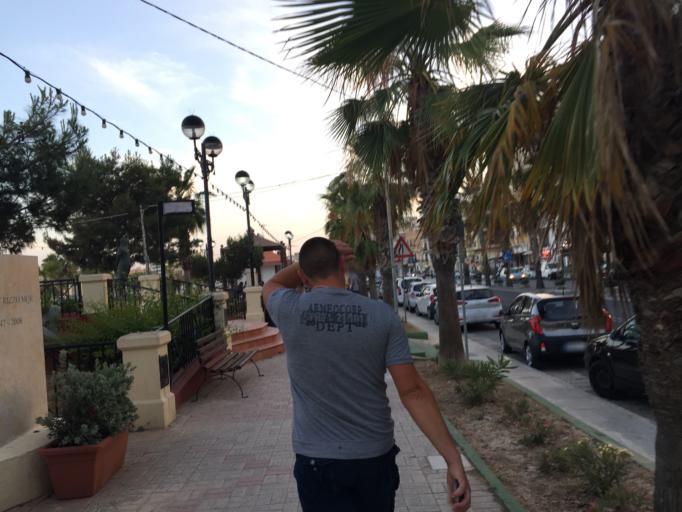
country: MT
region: Ta' Xbiex
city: Ta' Xbiex
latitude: 35.9056
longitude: 14.4970
